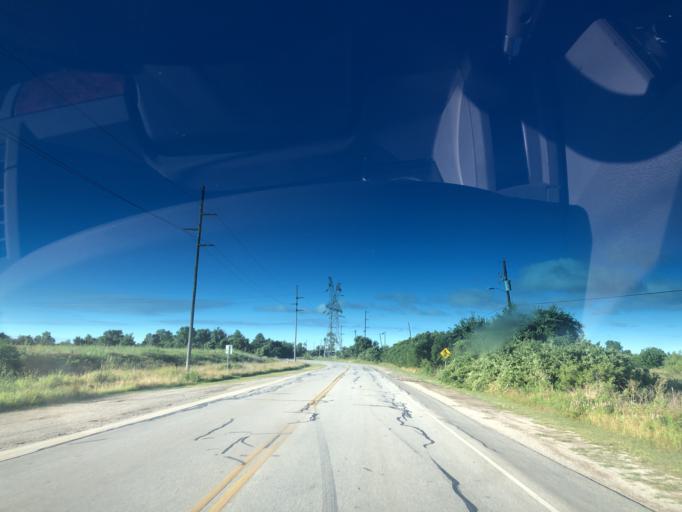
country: US
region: Texas
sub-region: Dallas County
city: Grand Prairie
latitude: 32.7872
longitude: -97.0172
